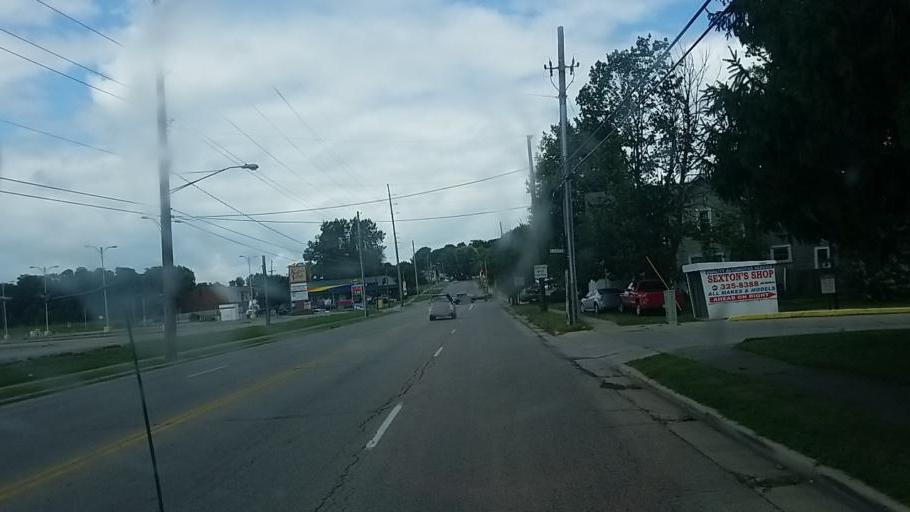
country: US
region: Ohio
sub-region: Clark County
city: Springfield
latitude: 39.9039
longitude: -83.7916
